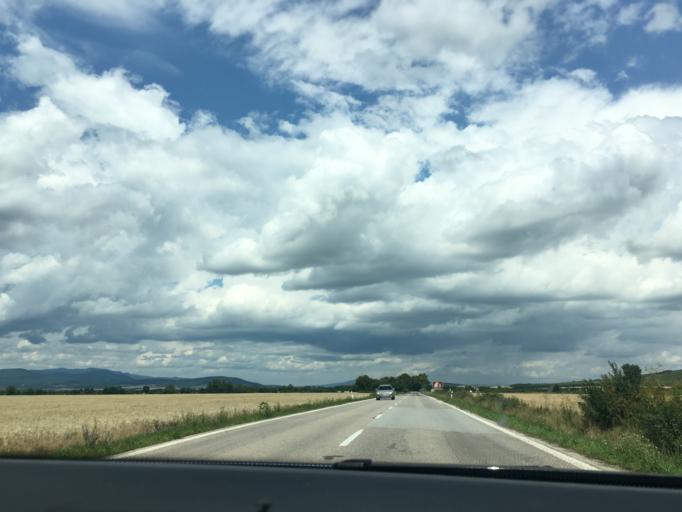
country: HU
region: Borsod-Abauj-Zemplen
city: Satoraljaujhely
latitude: 48.4408
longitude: 21.6548
